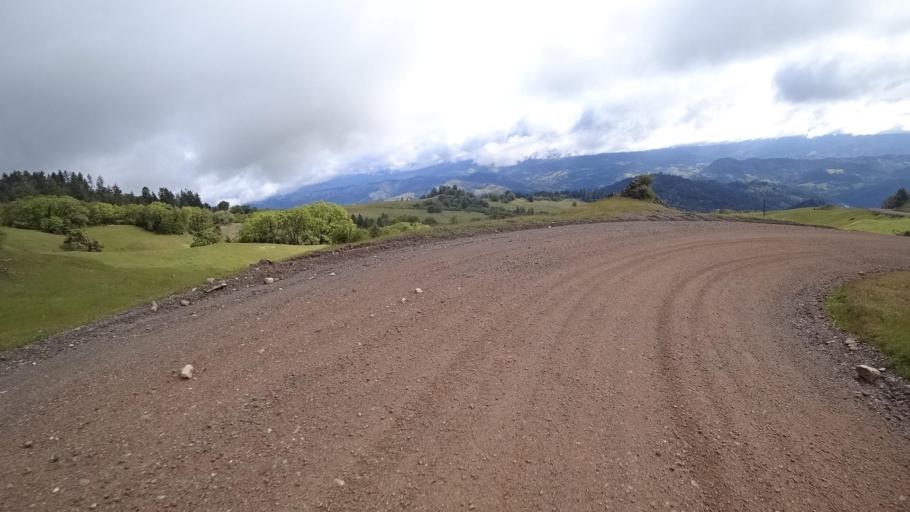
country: US
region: California
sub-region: Humboldt County
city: Redway
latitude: 40.2010
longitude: -123.6987
